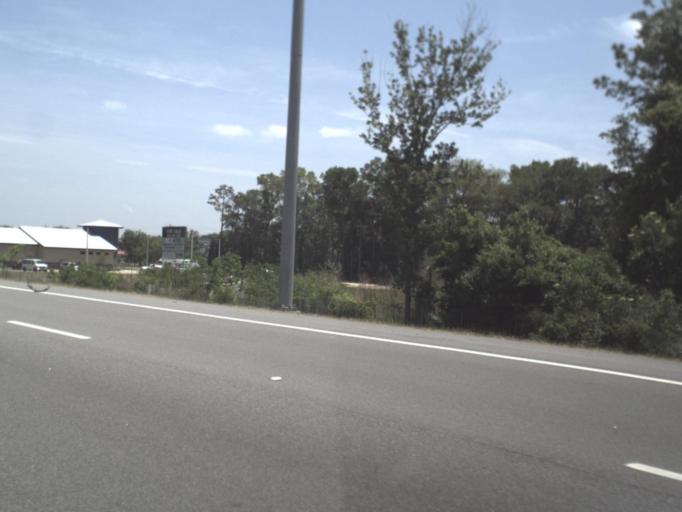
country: US
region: Florida
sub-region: Clay County
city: Bellair-Meadowbrook Terrace
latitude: 30.1911
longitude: -81.7228
